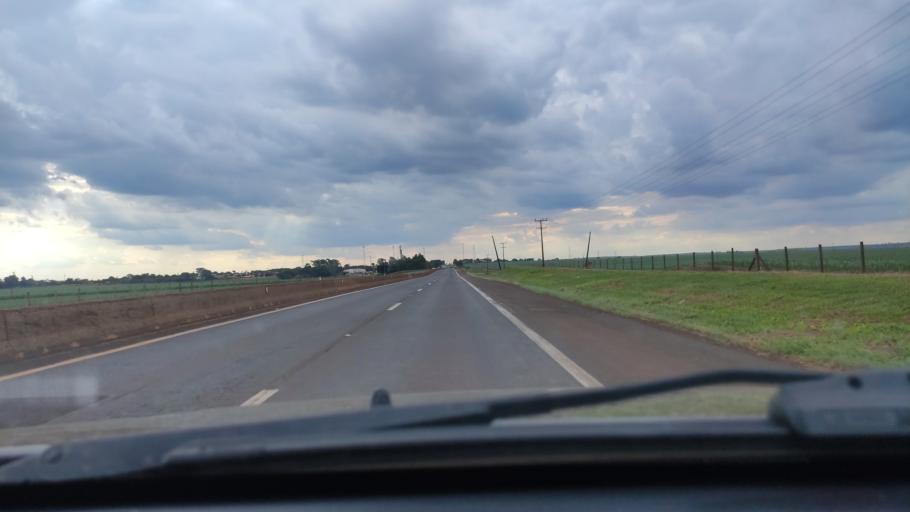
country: BR
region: Sao Paulo
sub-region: Palmital
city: Palmital
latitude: -22.8173
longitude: -50.0502
